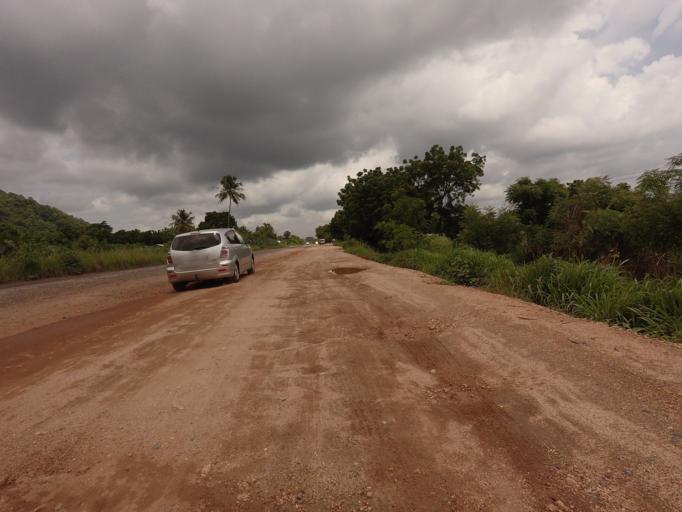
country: GH
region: Volta
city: Ho
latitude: 6.6505
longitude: 0.3005
